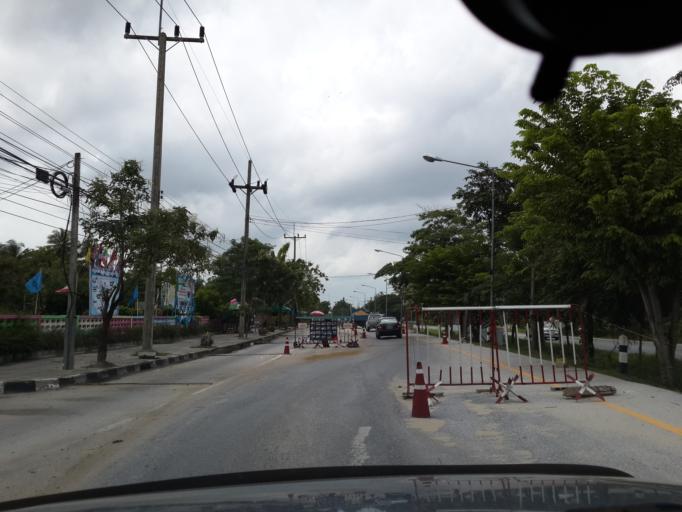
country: TH
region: Pattani
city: Pattani
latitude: 6.8732
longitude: 101.2995
